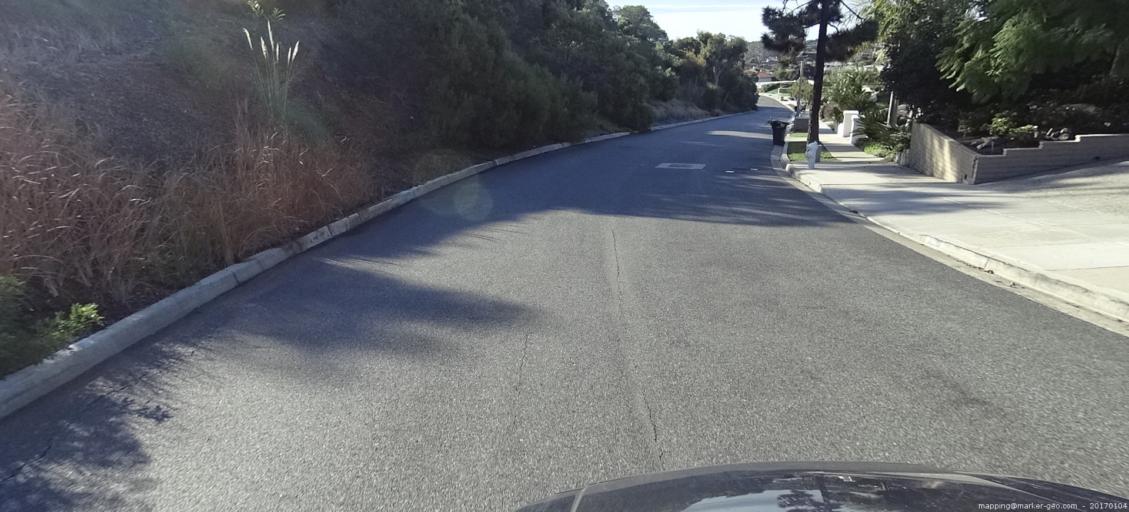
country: US
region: California
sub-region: Orange County
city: Dana Point
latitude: 33.4909
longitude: -117.7256
